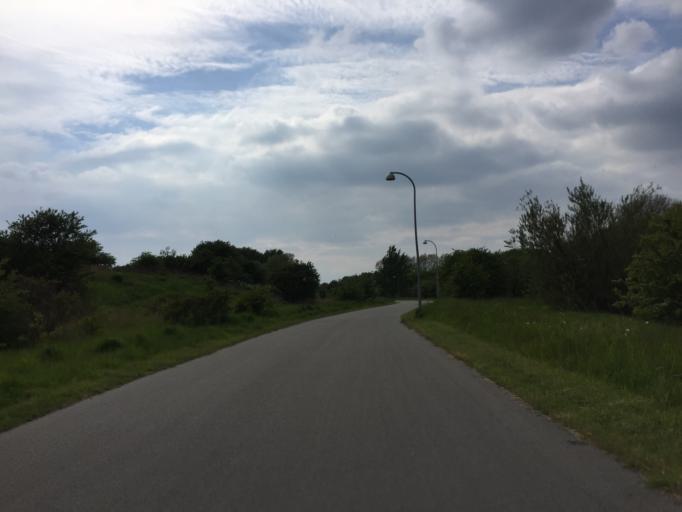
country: DK
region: Capital Region
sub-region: Hvidovre Kommune
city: Hvidovre
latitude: 55.6167
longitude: 12.4552
